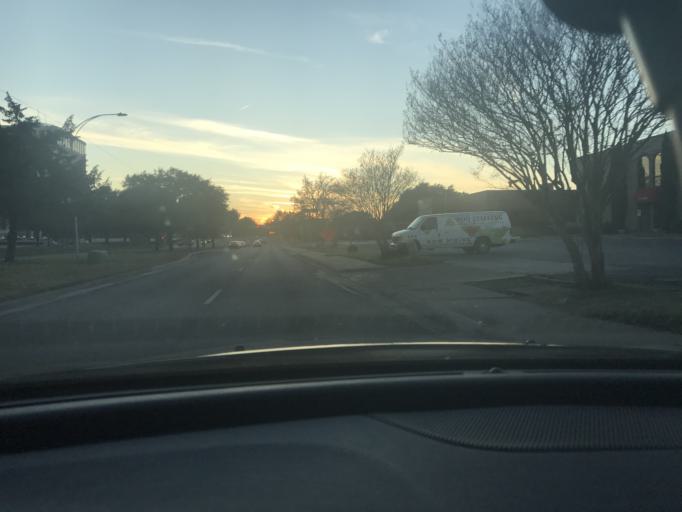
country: US
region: Texas
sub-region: Tarrant County
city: Arlington
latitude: 32.7649
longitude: -97.1009
